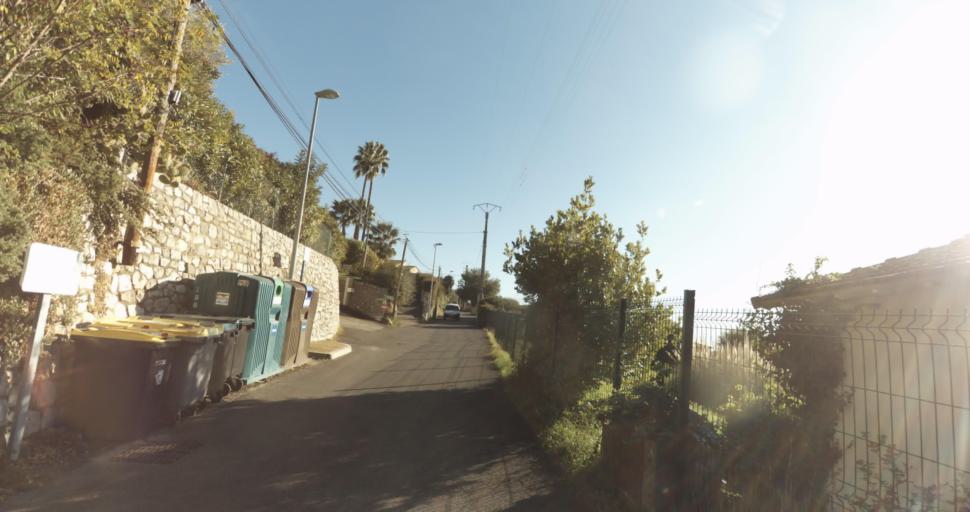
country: FR
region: Provence-Alpes-Cote d'Azur
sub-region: Departement des Alpes-Maritimes
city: La Gaude
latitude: 43.7163
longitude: 7.1326
